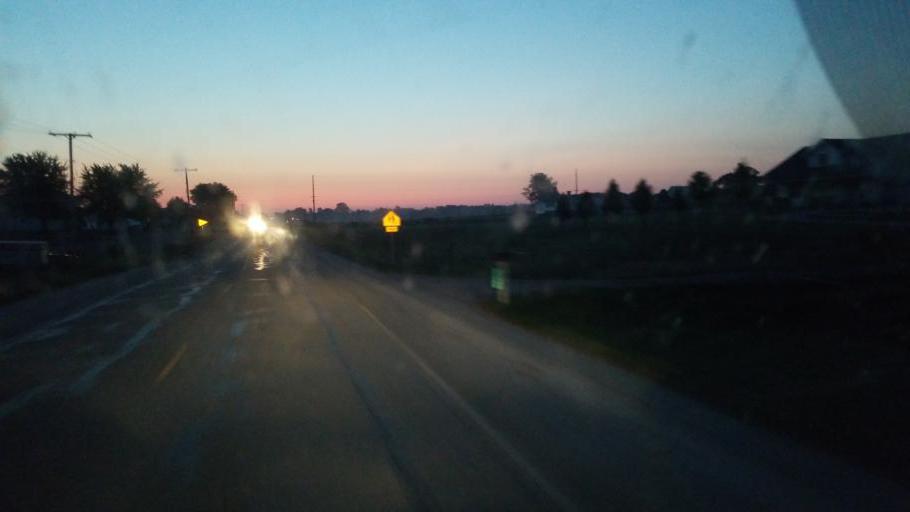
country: US
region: Indiana
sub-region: Elkhart County
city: Middlebury
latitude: 41.6757
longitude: -85.6517
